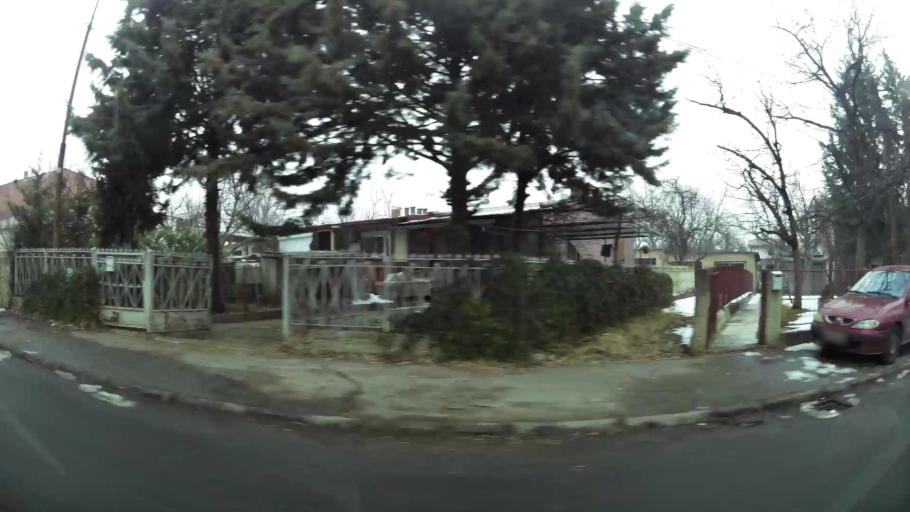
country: MK
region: Cair
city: Cair
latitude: 42.0166
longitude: 21.4577
